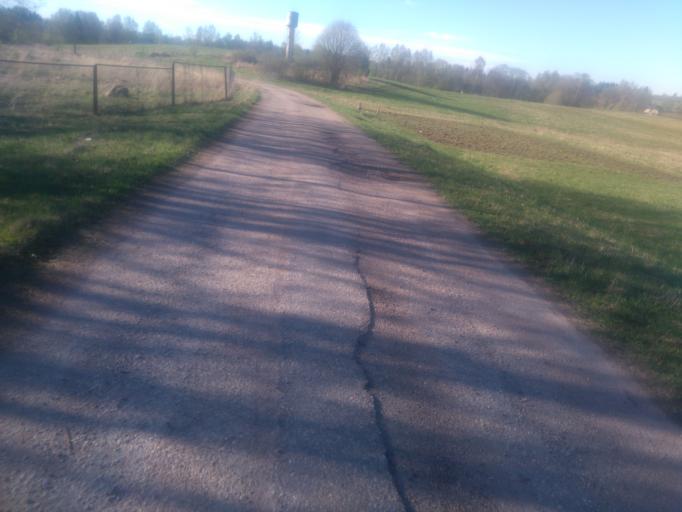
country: LV
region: Vecpiebalga
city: Vecpiebalga
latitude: 57.0203
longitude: 25.8517
